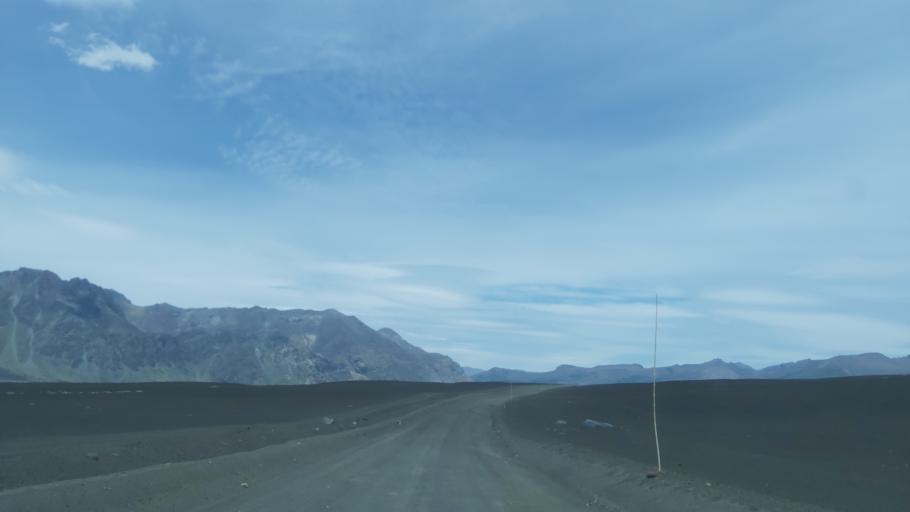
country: AR
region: Neuquen
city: Andacollo
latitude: -37.4297
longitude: -71.2862
